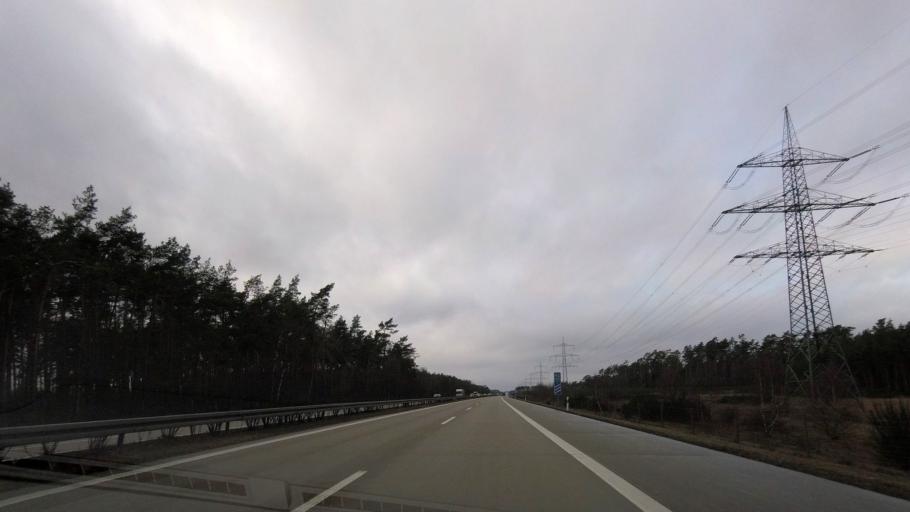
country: DE
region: Mecklenburg-Vorpommern
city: Zarrentin
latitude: 53.5113
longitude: 10.9064
